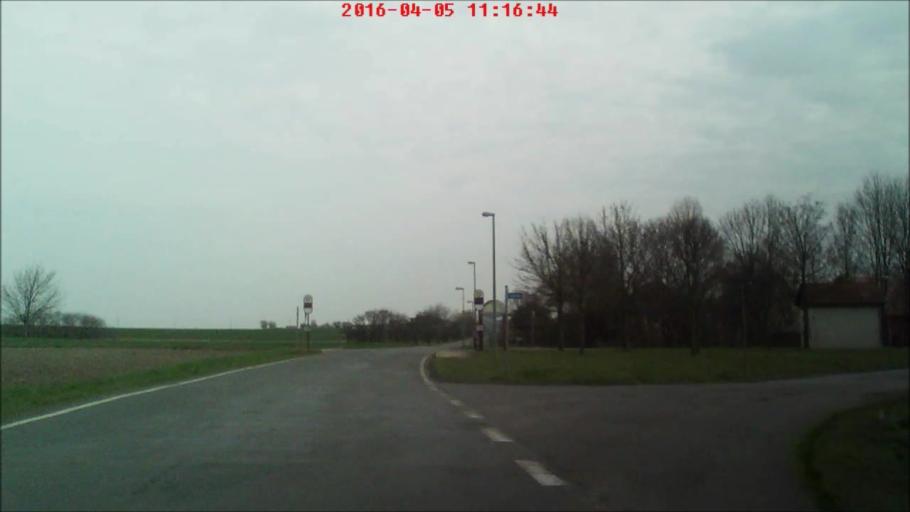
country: DE
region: Thuringia
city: Zimmernsupra
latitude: 50.9899
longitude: 10.9236
